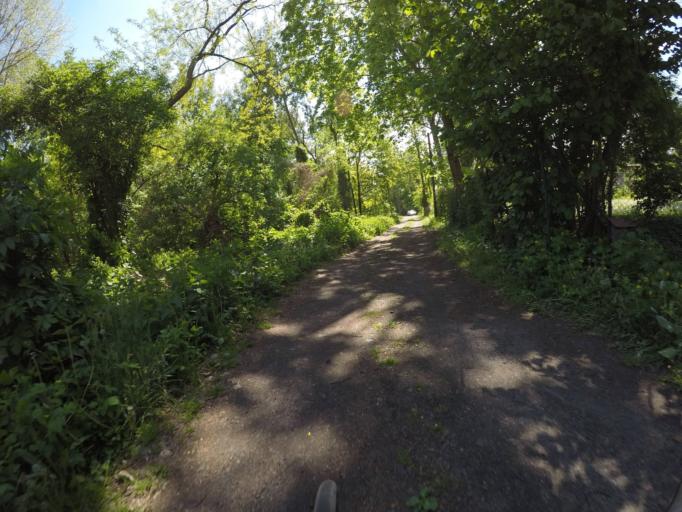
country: DE
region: Brandenburg
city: Werder
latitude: 52.3944
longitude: 12.9395
